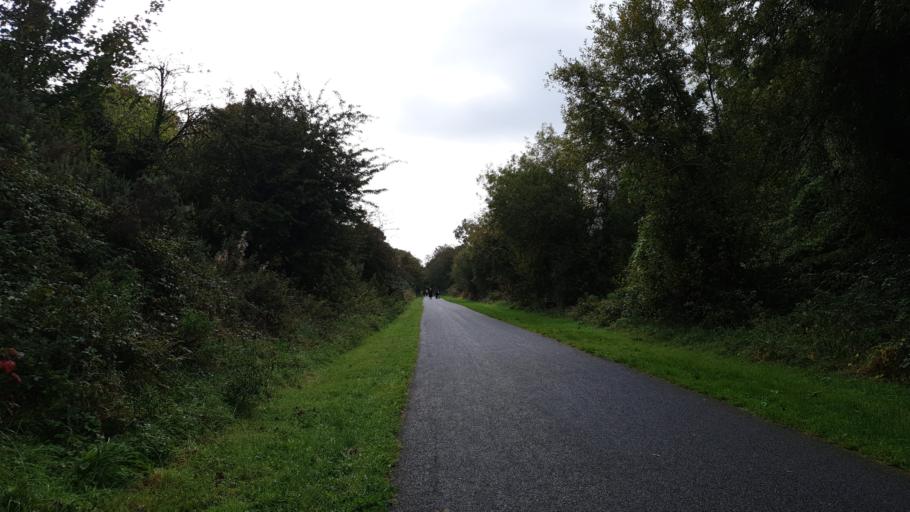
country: IE
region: Munster
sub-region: County Cork
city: Cork
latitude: 51.8931
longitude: -8.4148
